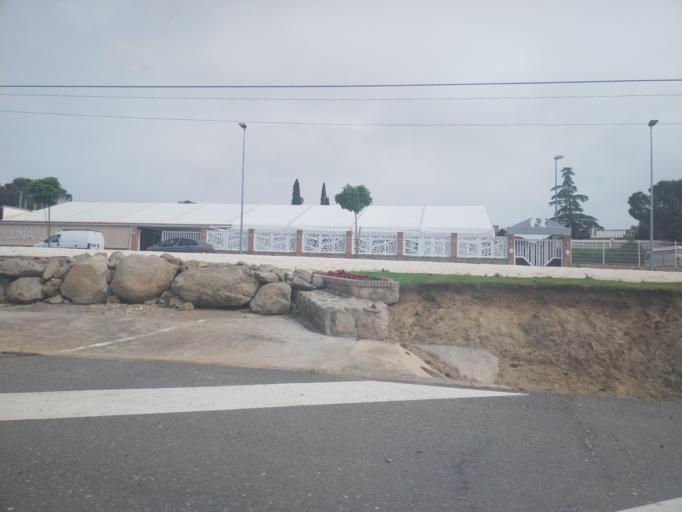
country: ES
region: Castille-La Mancha
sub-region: Province of Toledo
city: Guadamur
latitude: 39.8020
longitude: -4.1365
